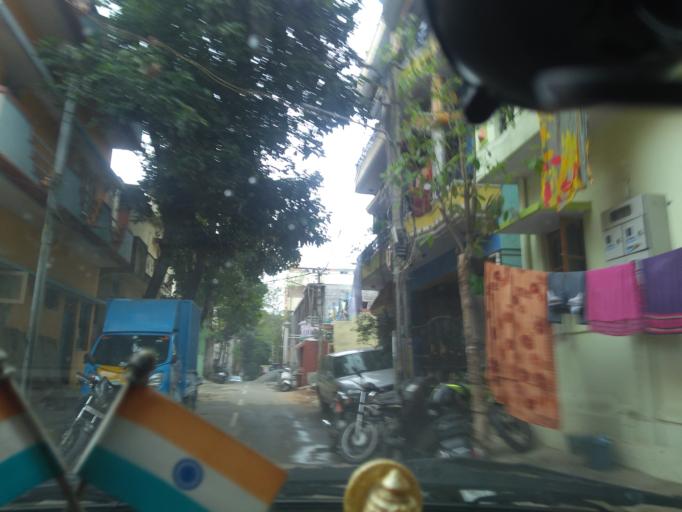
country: IN
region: Karnataka
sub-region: Bangalore Urban
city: Bangalore
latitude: 13.0104
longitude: 77.5590
